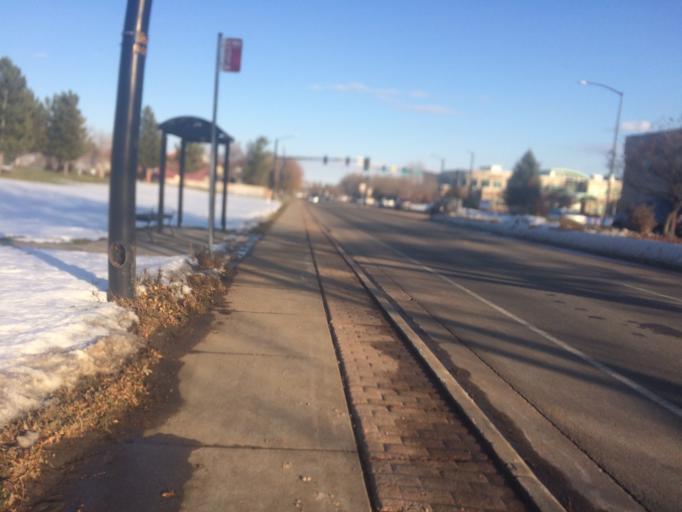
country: US
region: Colorado
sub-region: Boulder County
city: Lafayette
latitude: 39.9871
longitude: -105.1046
